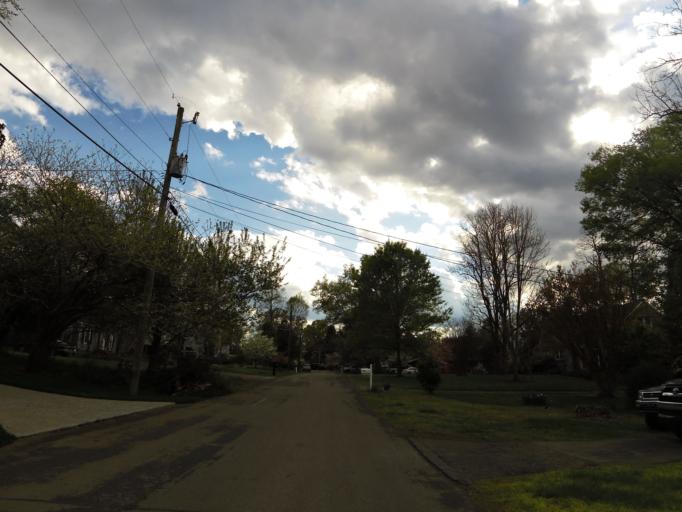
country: US
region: Tennessee
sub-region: Blount County
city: Maryville
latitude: 35.7447
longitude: -83.9810
